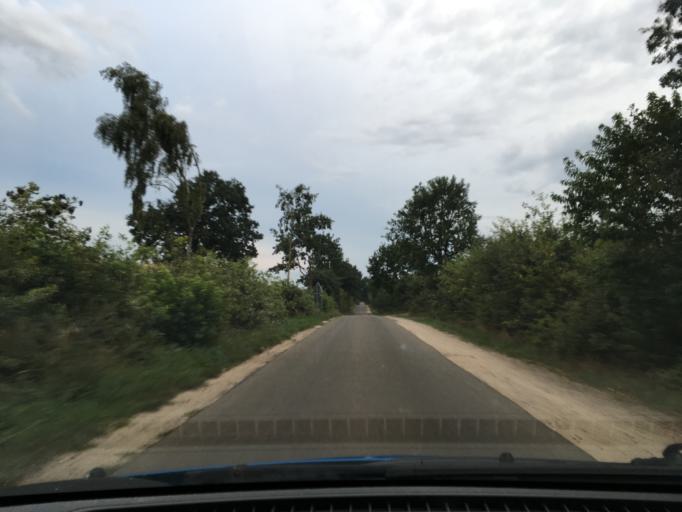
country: DE
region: Schleswig-Holstein
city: Lanze
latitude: 53.4092
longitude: 10.6067
